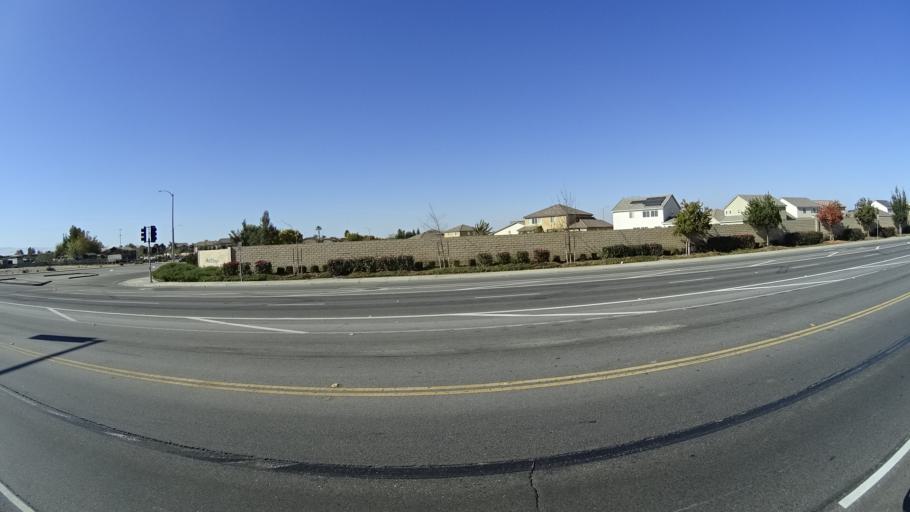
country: US
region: California
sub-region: Kern County
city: Greenfield
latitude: 35.2818
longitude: -119.0567
